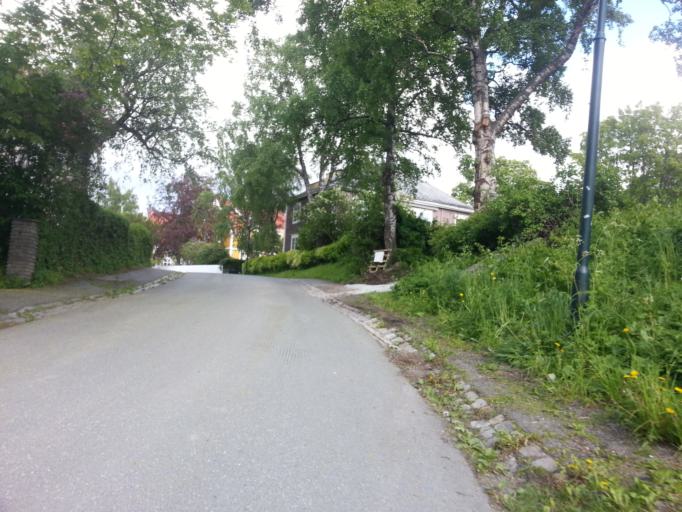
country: NO
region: Sor-Trondelag
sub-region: Trondheim
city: Trondheim
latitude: 63.4216
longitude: 10.4051
